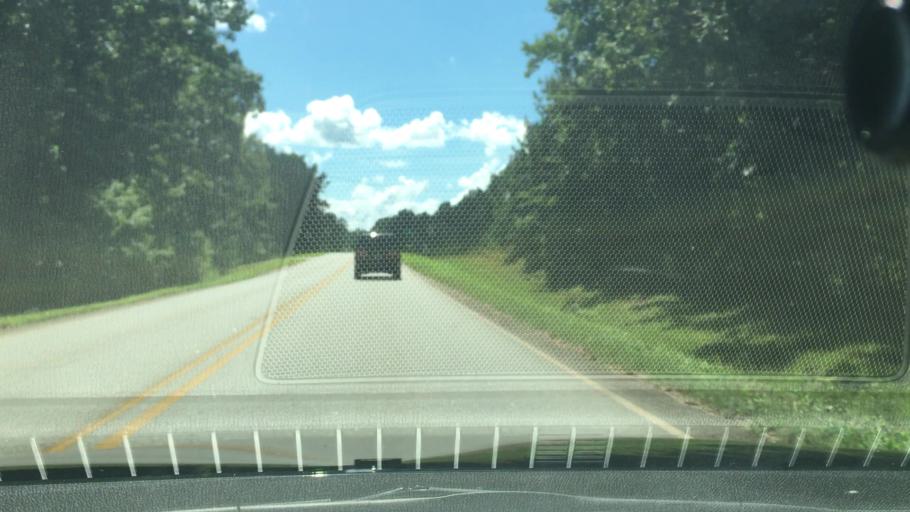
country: US
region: Georgia
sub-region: Jasper County
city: Monticello
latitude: 33.3001
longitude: -83.6616
